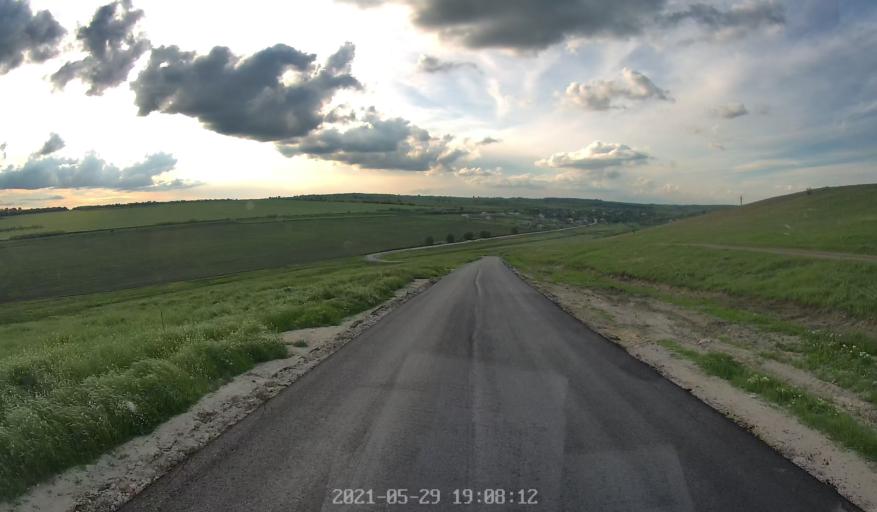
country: MD
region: Chisinau
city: Singera
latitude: 46.8267
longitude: 28.9606
